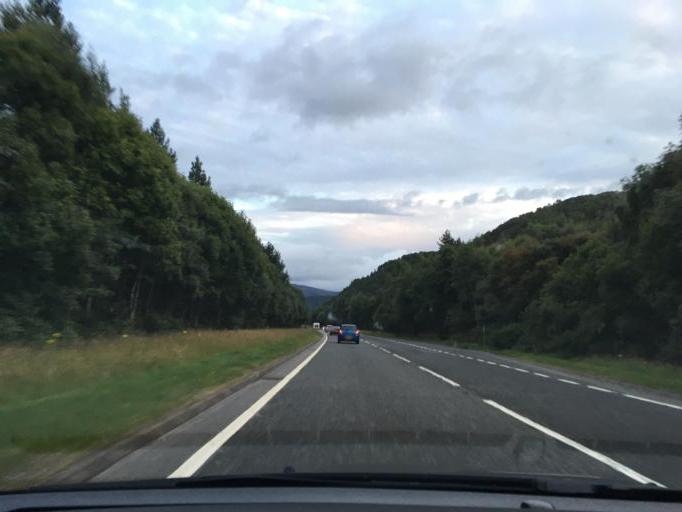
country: GB
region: Scotland
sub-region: Highland
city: Aviemore
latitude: 57.1906
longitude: -3.8369
